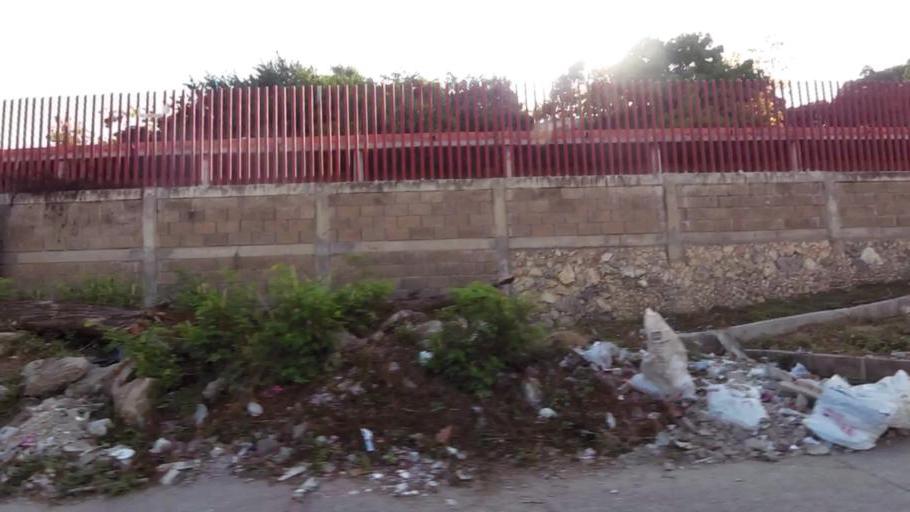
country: CO
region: Bolivar
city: Cartagena
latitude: 10.3979
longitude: -75.5203
